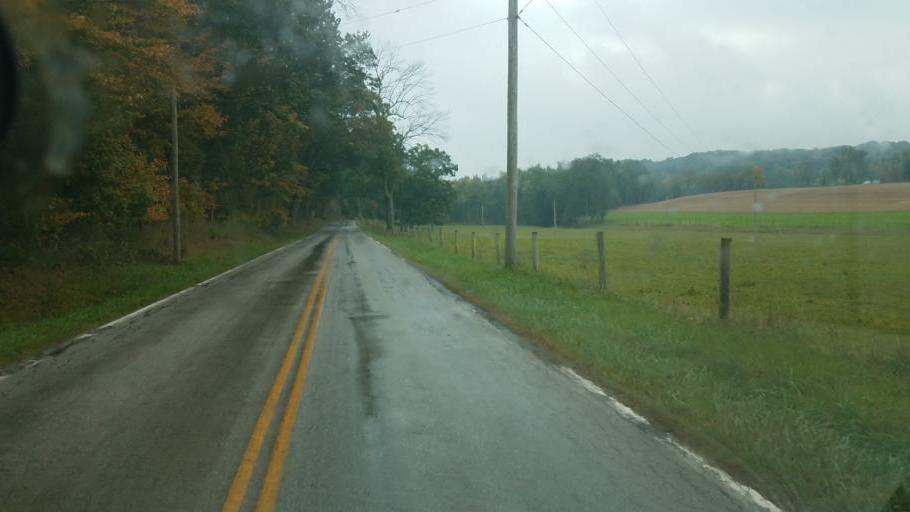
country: US
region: Ohio
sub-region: Sandusky County
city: Bellville
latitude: 40.6579
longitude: -82.3976
